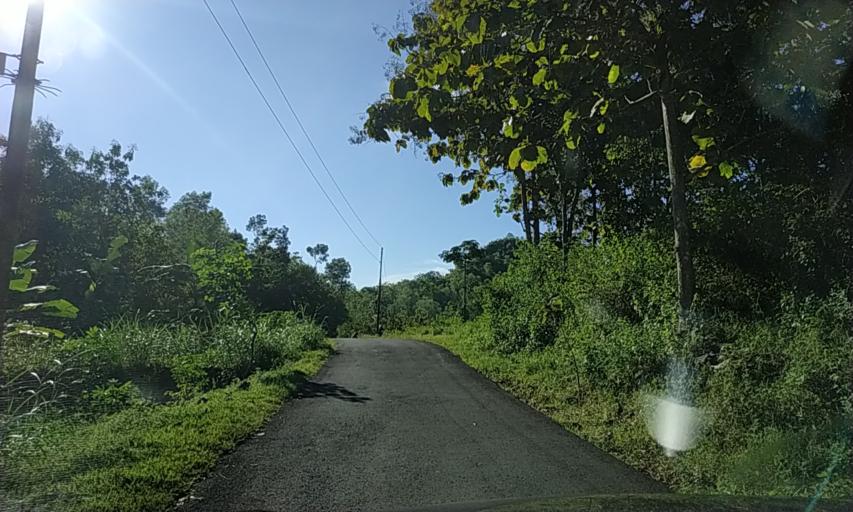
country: ID
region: East Java
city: Krajan
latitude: -8.1224
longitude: 110.8809
